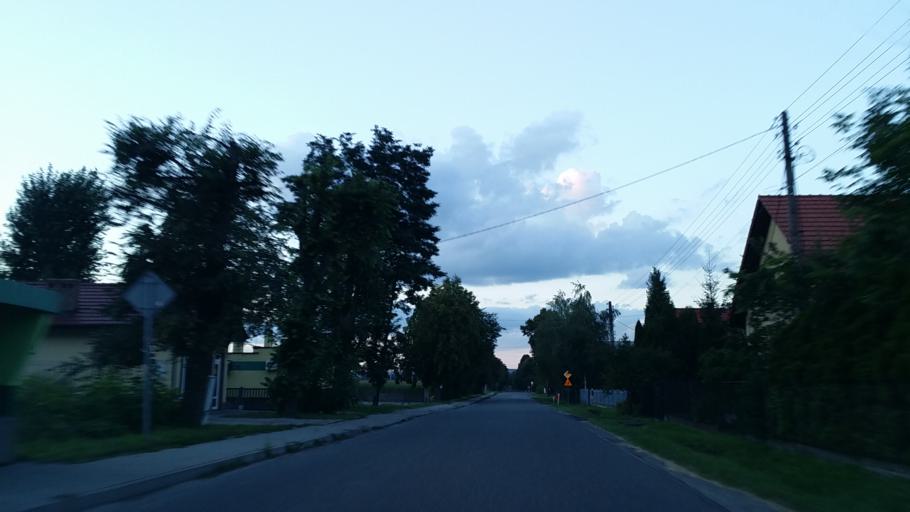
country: PL
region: Lesser Poland Voivodeship
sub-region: Powiat oswiecimski
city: Przeciszow
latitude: 50.0204
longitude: 19.3742
